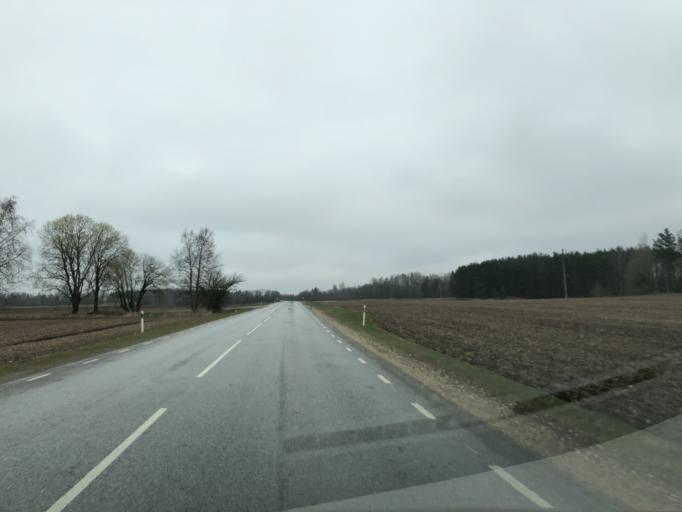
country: EE
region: Laeaene-Virumaa
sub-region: Rakke vald
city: Rakke
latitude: 58.9510
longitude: 26.2717
